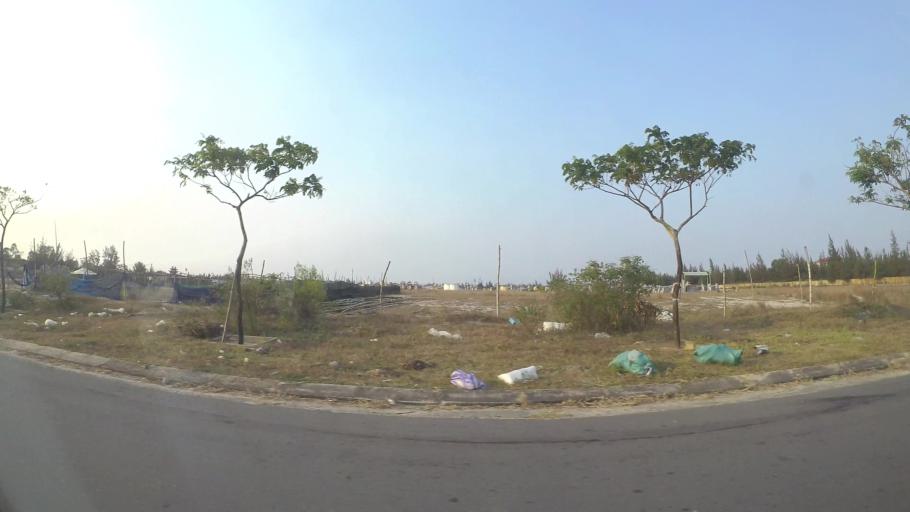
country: VN
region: Da Nang
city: Ngu Hanh Son
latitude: 15.9779
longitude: 108.2421
